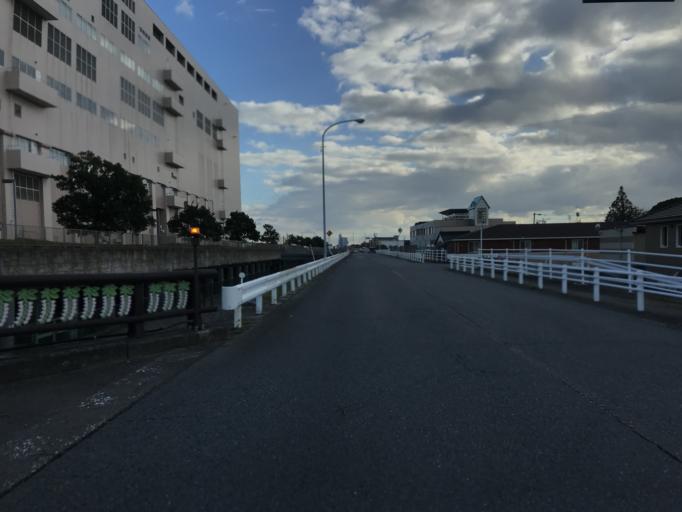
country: JP
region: Aichi
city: Nagoya-shi
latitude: 35.1900
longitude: 136.8433
